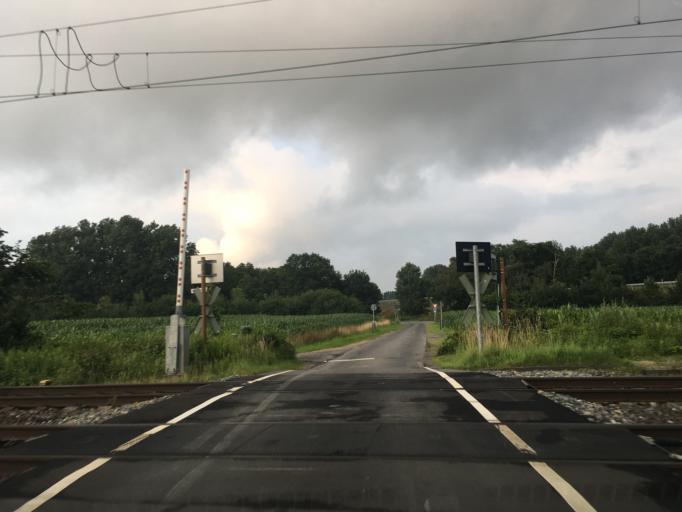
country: DE
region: North Rhine-Westphalia
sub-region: Regierungsbezirk Munster
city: Greven
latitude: 52.0526
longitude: 7.6127
